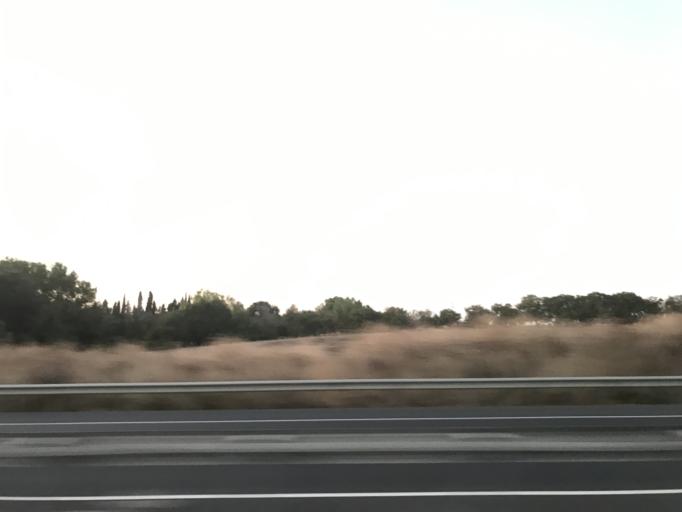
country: TR
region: Tekirdag
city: Tekirdag
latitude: 41.0004
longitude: 27.6610
